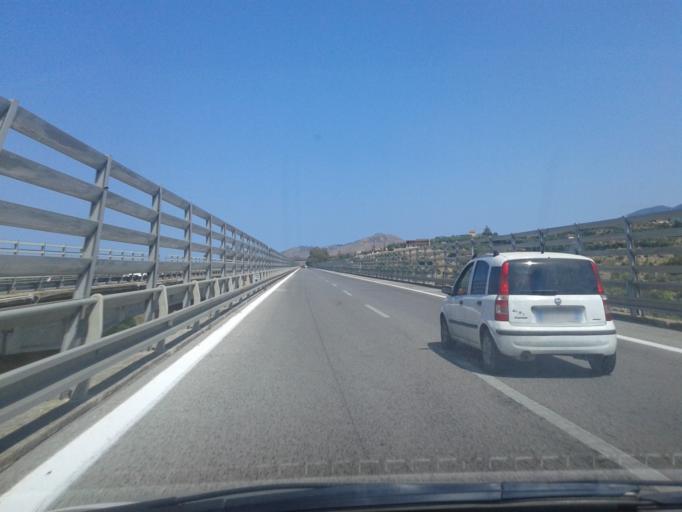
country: IT
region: Sicily
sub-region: Palermo
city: Campofelice di Roccella
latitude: 37.9865
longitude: 13.8895
